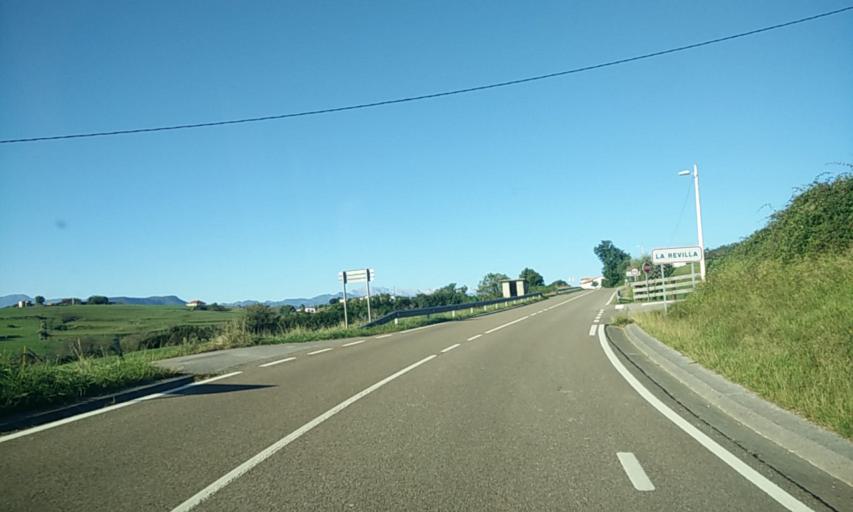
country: ES
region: Cantabria
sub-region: Provincia de Cantabria
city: San Vicente de la Barquera
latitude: 43.3818
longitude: -4.3544
